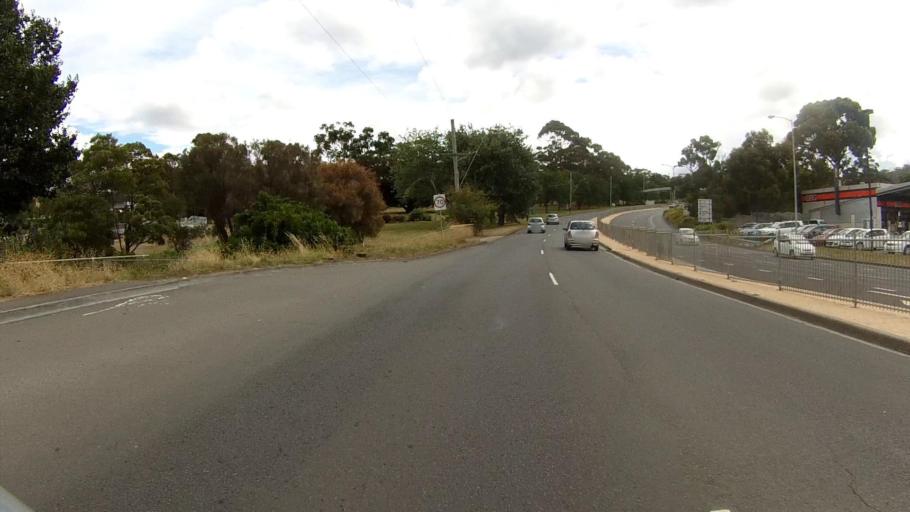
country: AU
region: Tasmania
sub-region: Clarence
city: Bellerive
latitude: -42.8684
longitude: 147.3675
